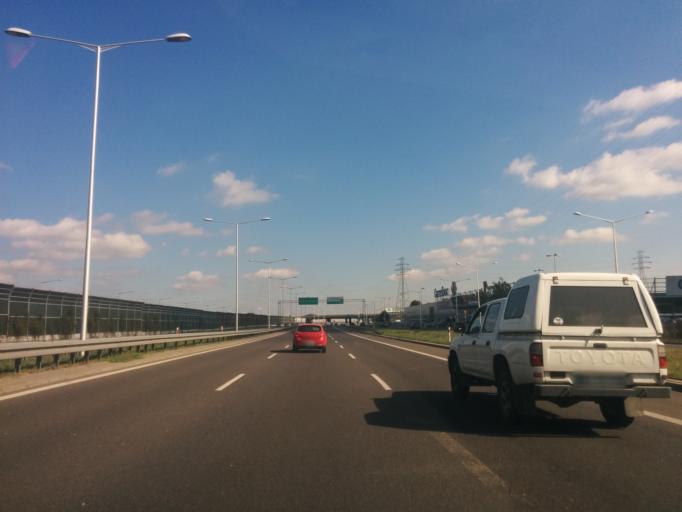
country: PL
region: Masovian Voivodeship
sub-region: Warszawa
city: Targowek
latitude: 52.3051
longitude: 21.0547
